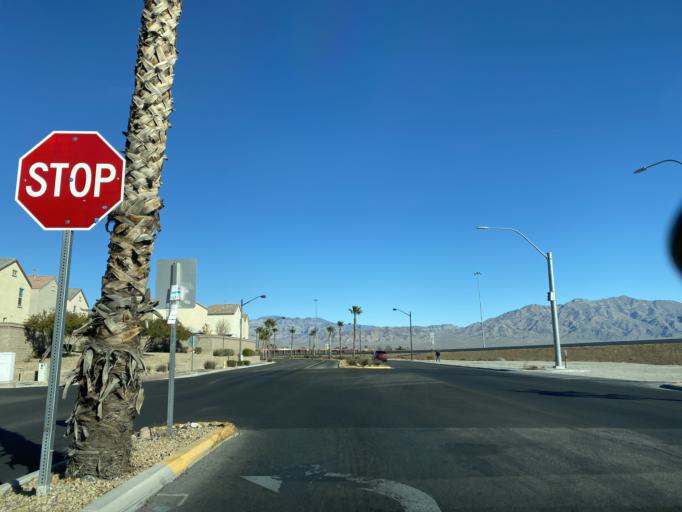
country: US
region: Nevada
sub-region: Clark County
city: Summerlin South
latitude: 36.2989
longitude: -115.2892
